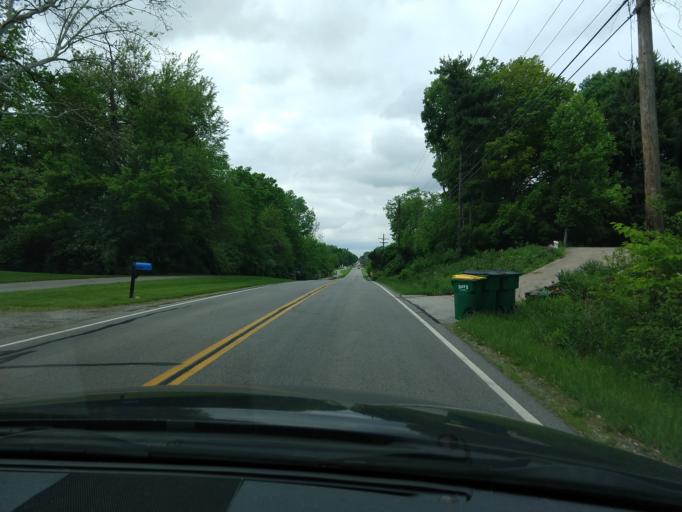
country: US
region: Indiana
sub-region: Hamilton County
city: Westfield
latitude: 40.0182
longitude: -86.1275
